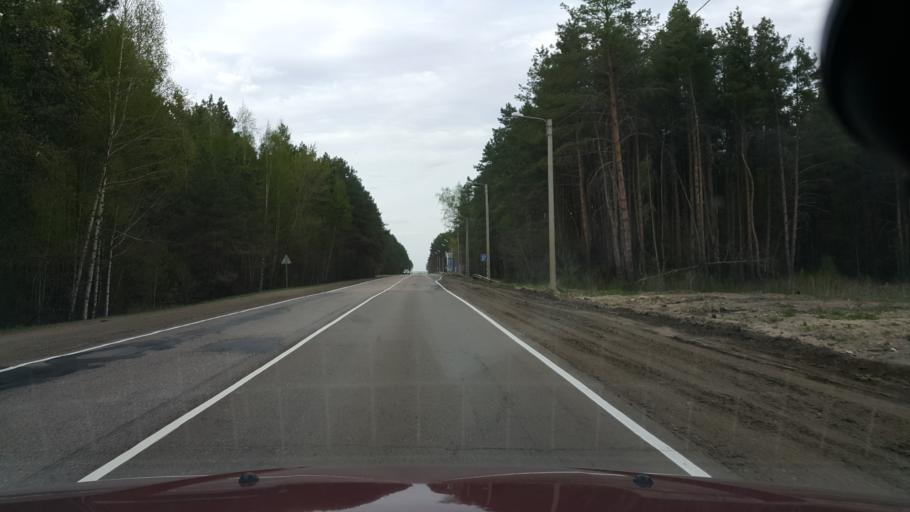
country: RU
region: Tambov
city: Pokrovo-Prigorodnoye
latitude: 52.5849
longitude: 41.3502
